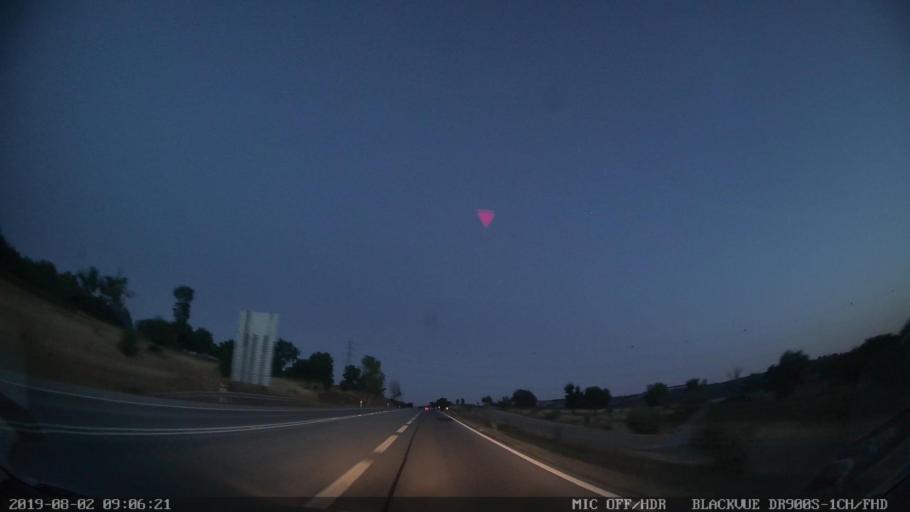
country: PT
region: Portalegre
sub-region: Nisa
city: Nisa
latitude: 39.5280
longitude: -7.7864
